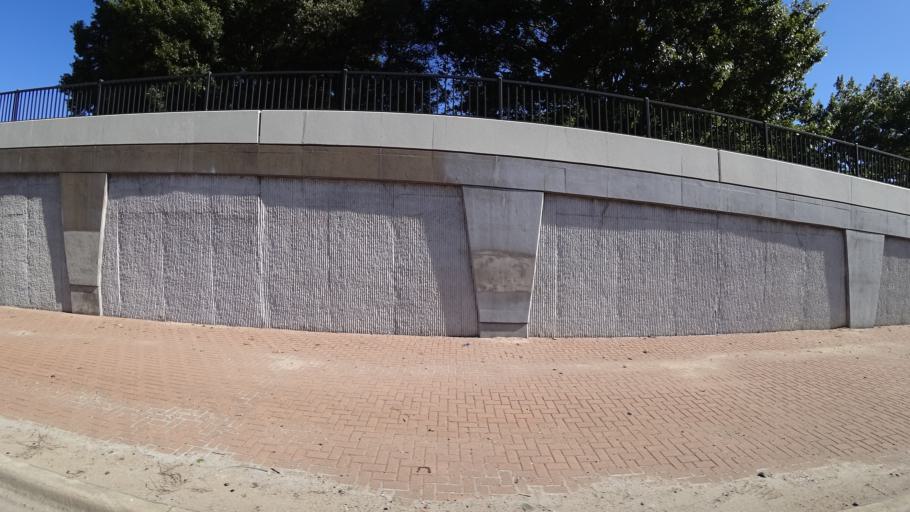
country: US
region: Texas
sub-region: Travis County
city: Austin
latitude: 30.3270
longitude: -97.6745
